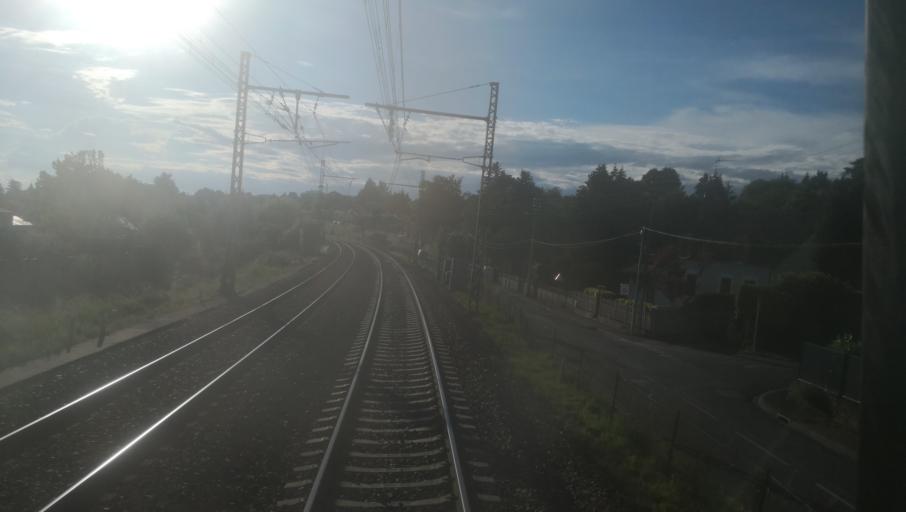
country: FR
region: Centre
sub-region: Departement du Cher
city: Vierzon
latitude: 47.2196
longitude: 2.0903
